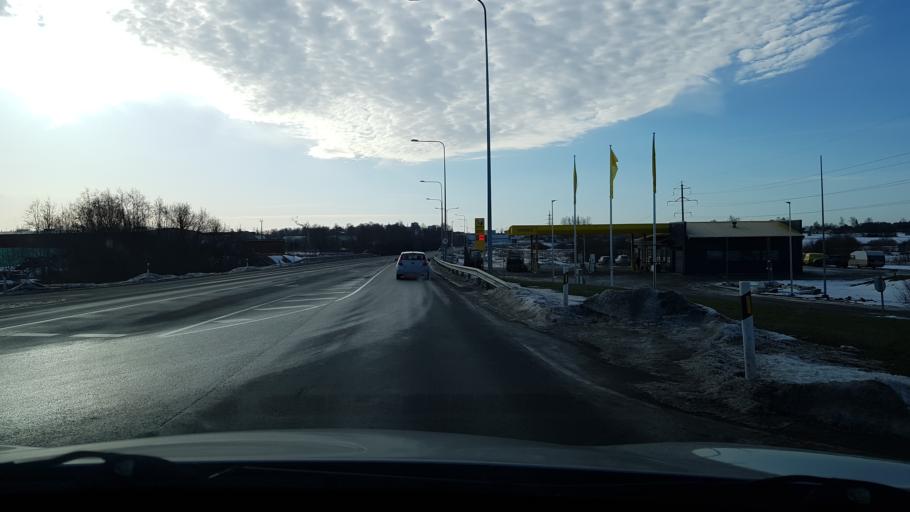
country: EE
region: Viljandimaa
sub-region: Viljandi linn
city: Viljandi
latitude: 58.3731
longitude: 25.5637
